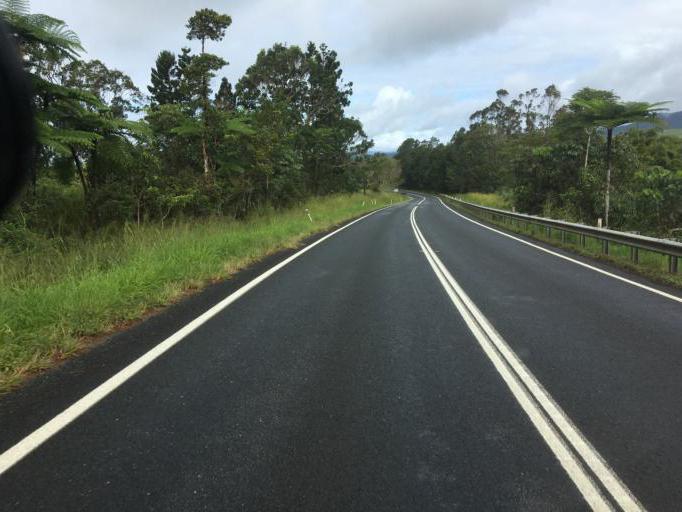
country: AU
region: Queensland
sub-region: Tablelands
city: Ravenshoe
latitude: -17.5236
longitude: 145.6453
